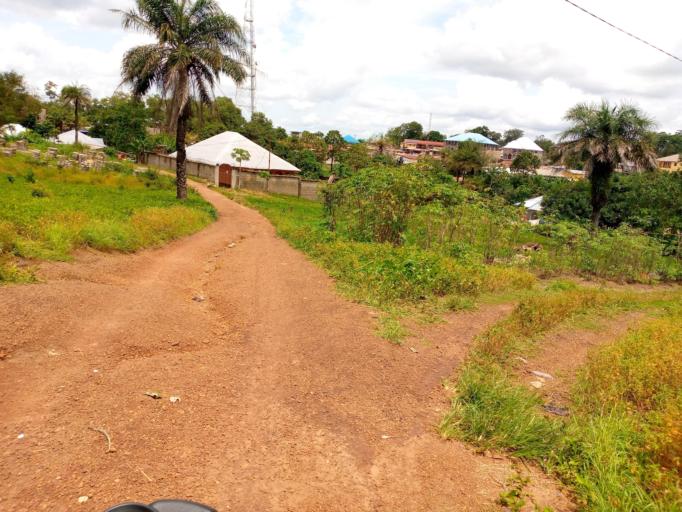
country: SL
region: Northern Province
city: Magburaka
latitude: 8.7237
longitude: -11.9351
